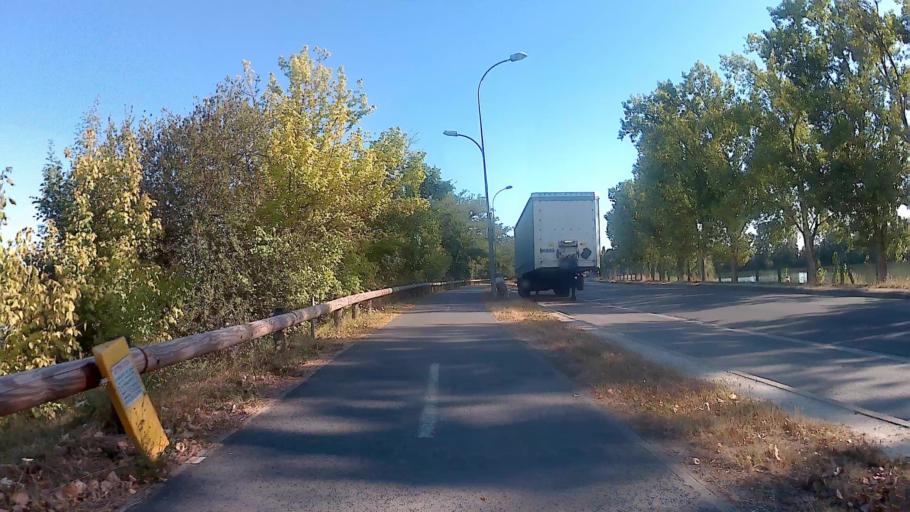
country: FR
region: Aquitaine
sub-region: Departement de la Gironde
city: Villenave-d'Ornon
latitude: 44.7845
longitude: -0.5362
